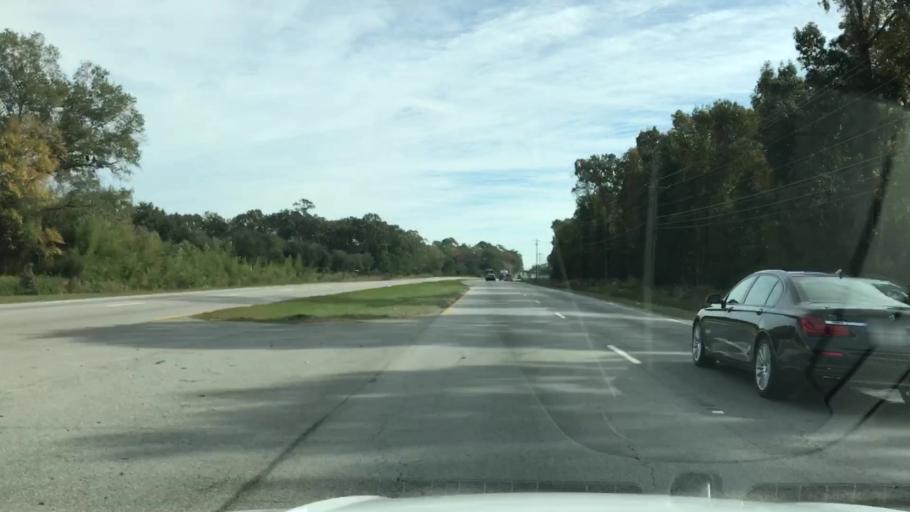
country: US
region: South Carolina
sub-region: Charleston County
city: Shell Point
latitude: 32.7946
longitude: -80.0632
